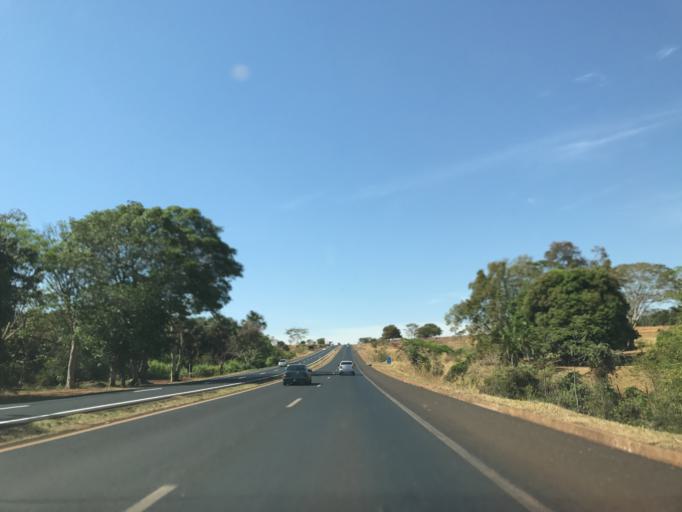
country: BR
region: Minas Gerais
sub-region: Centralina
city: Centralina
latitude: -18.6605
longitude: -49.1671
